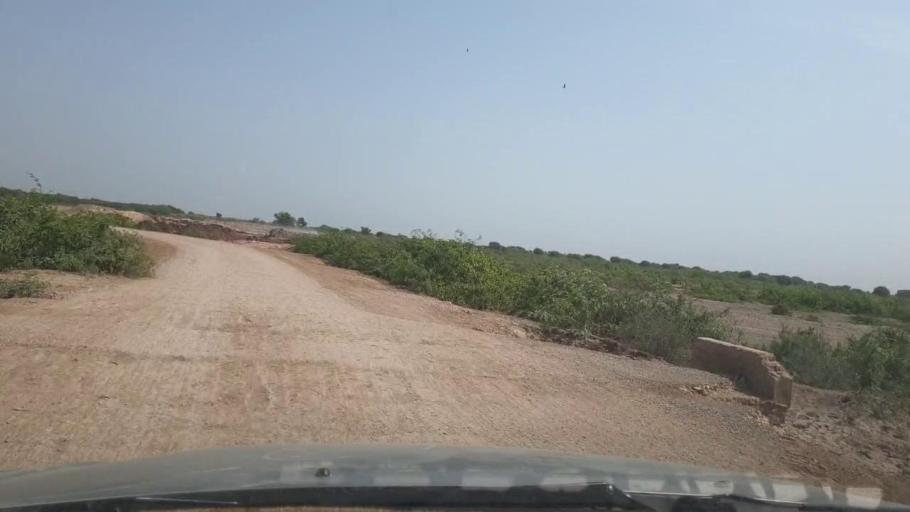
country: PK
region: Sindh
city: Tando Ghulam Ali
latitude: 25.1581
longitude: 68.8789
